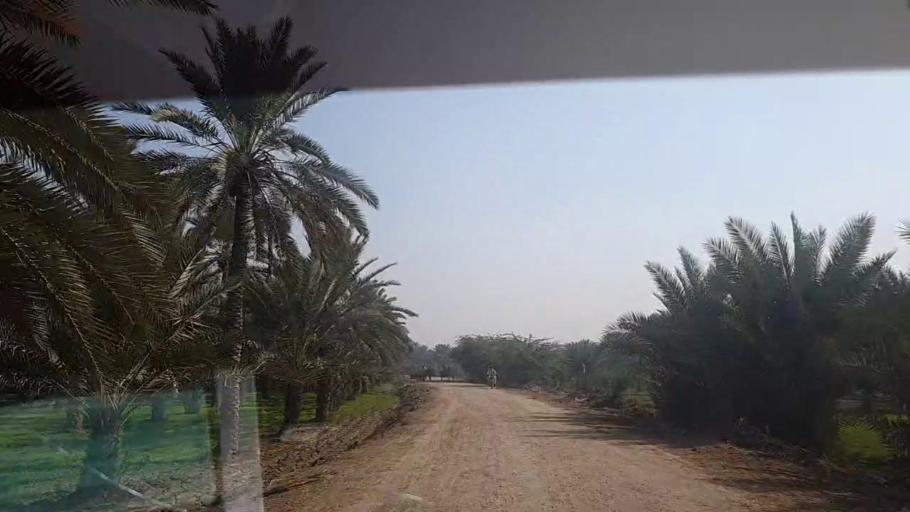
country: PK
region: Sindh
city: Kot Diji
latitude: 27.4337
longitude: 68.6883
